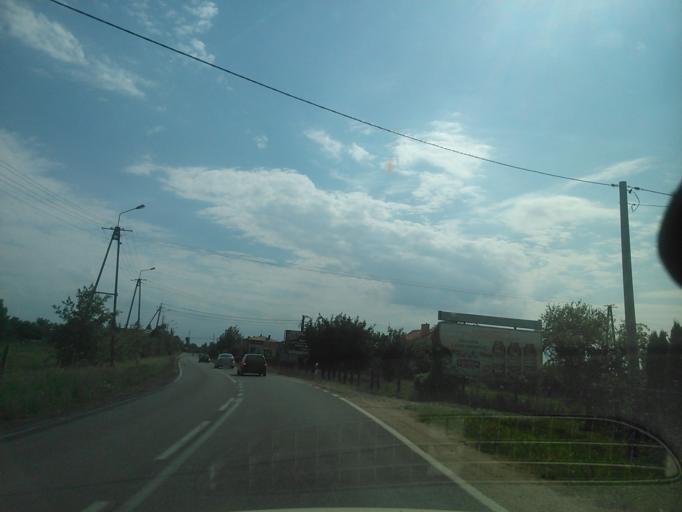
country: PL
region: Masovian Voivodeship
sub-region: Powiat mlawski
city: Mlawa
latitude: 53.1328
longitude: 20.3435
